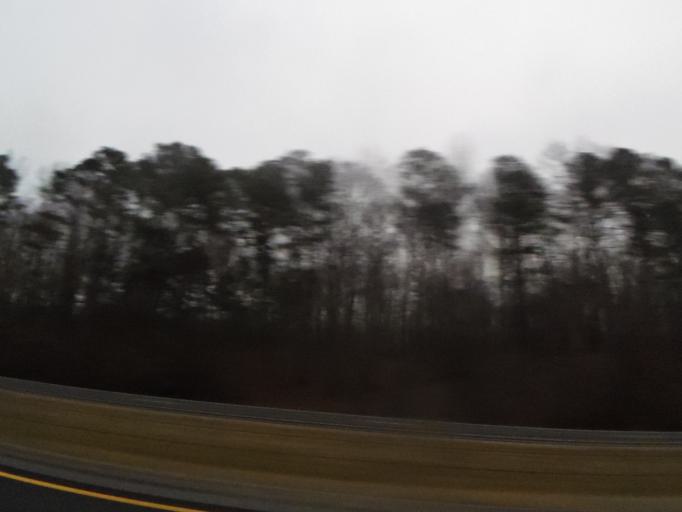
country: US
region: Alabama
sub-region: Cullman County
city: Cullman
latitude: 34.2216
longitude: -86.8759
